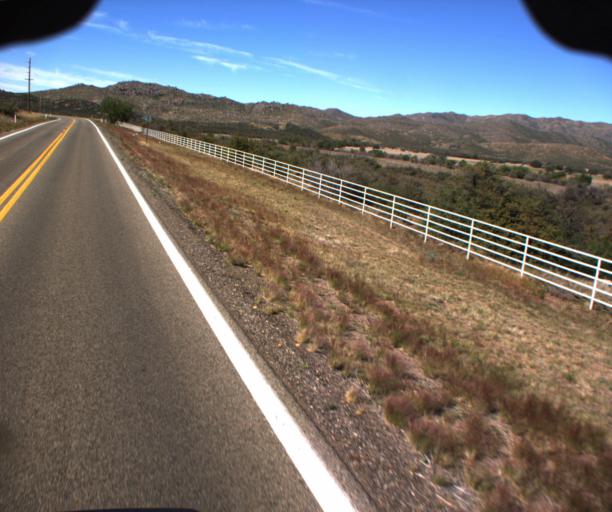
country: US
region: Arizona
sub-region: Yavapai County
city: Congress
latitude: 34.2544
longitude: -112.7336
